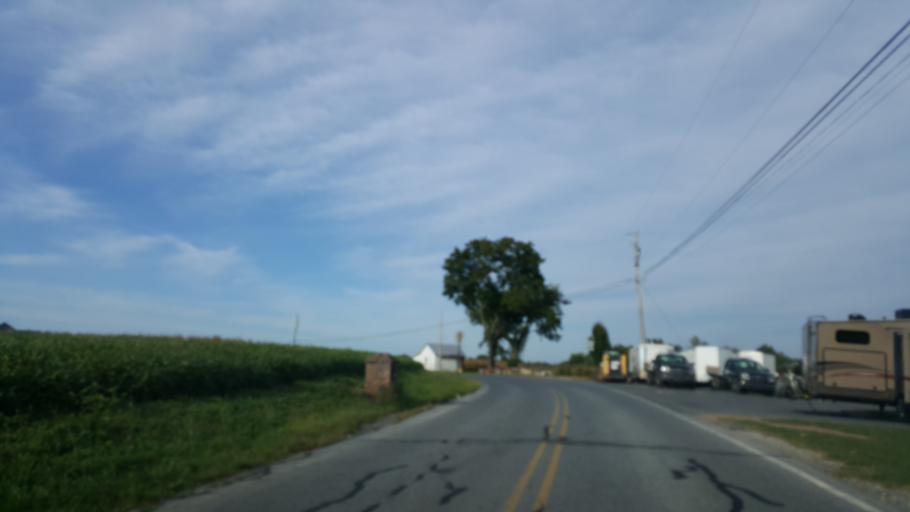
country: US
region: Pennsylvania
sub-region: Lebanon County
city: Campbelltown
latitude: 40.2662
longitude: -76.5684
